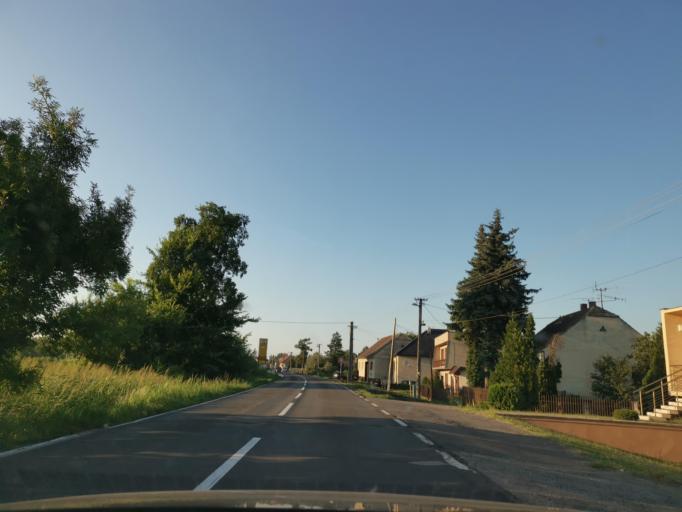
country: CZ
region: South Moravian
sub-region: Okres Breclav
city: Lanzhot
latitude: 48.6498
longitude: 17.0128
